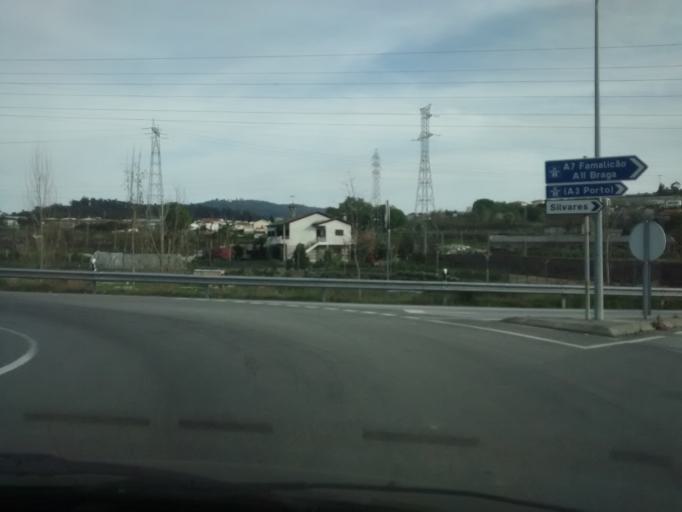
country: PT
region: Braga
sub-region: Guimaraes
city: Ponte
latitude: 41.4628
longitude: -8.3208
